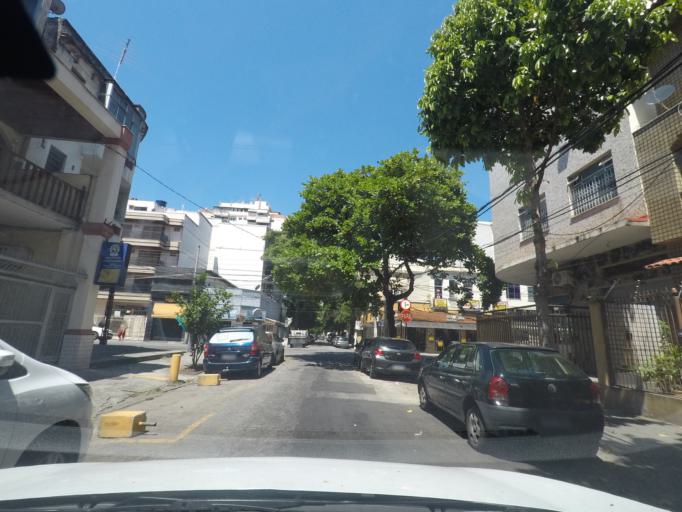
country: BR
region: Rio de Janeiro
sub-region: Rio De Janeiro
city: Rio de Janeiro
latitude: -22.9189
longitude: -43.2397
